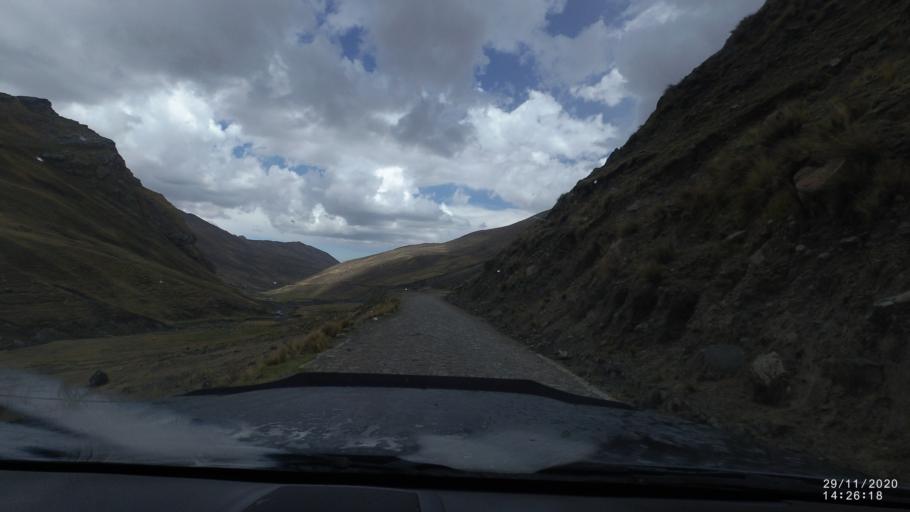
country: BO
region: Cochabamba
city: Sipe Sipe
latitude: -17.2569
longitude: -66.3716
